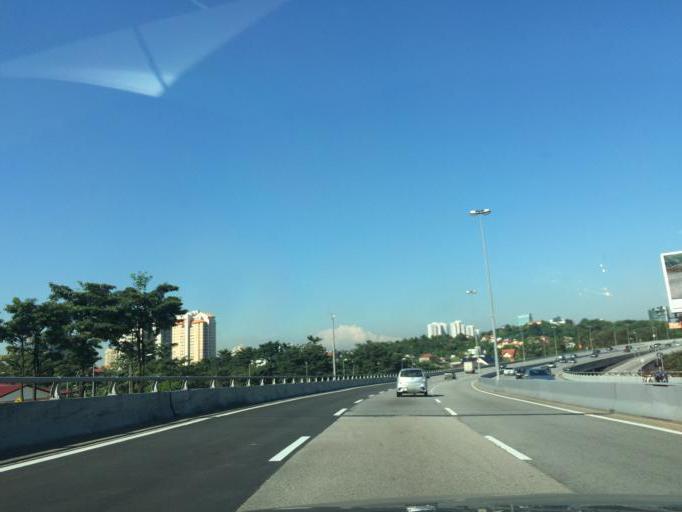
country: MY
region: Selangor
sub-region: Petaling
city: Petaling Jaya
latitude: 3.1601
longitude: 101.6281
